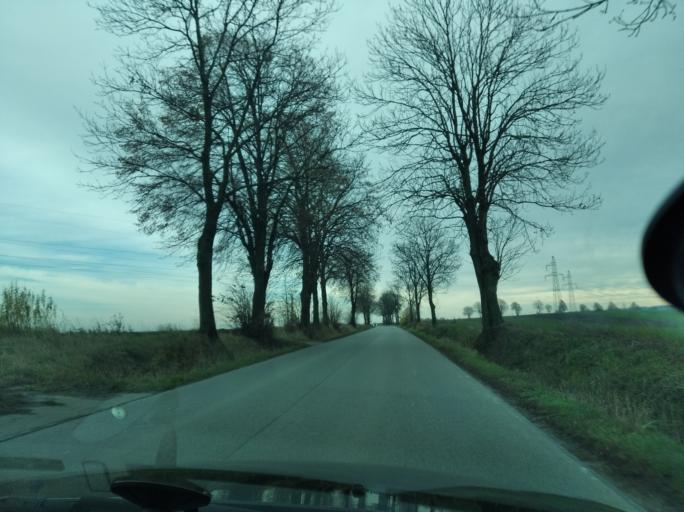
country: PL
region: Subcarpathian Voivodeship
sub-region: Powiat lancucki
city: Wysoka
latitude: 50.0251
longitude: 22.2545
